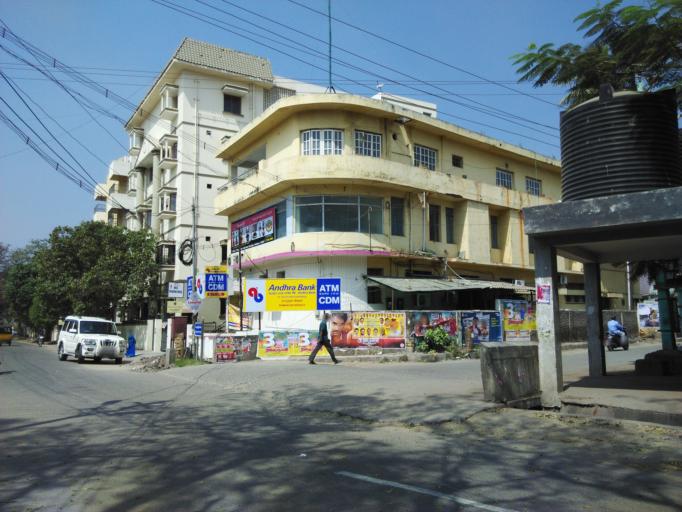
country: IN
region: Tamil Nadu
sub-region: Coimbatore
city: Coimbatore
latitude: 11.0141
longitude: 76.9649
